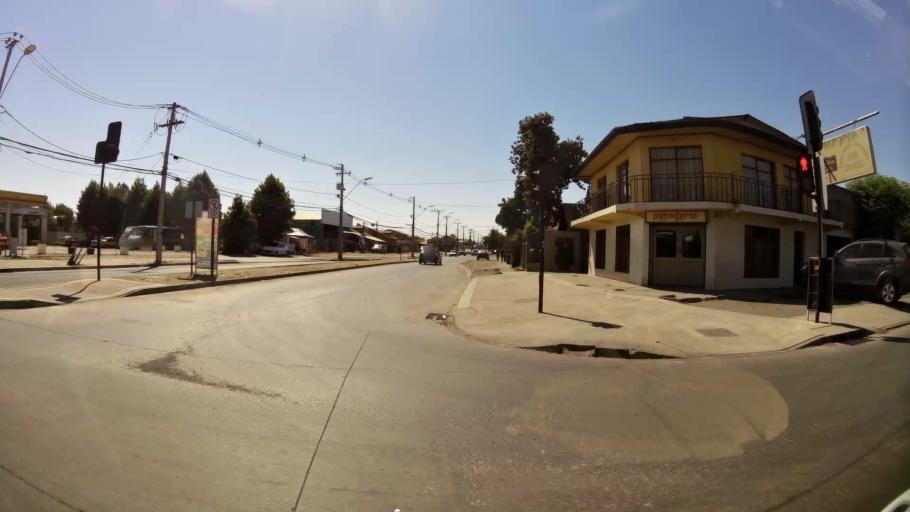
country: CL
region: Maule
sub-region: Provincia de Curico
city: Curico
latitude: -34.9693
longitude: -71.2482
